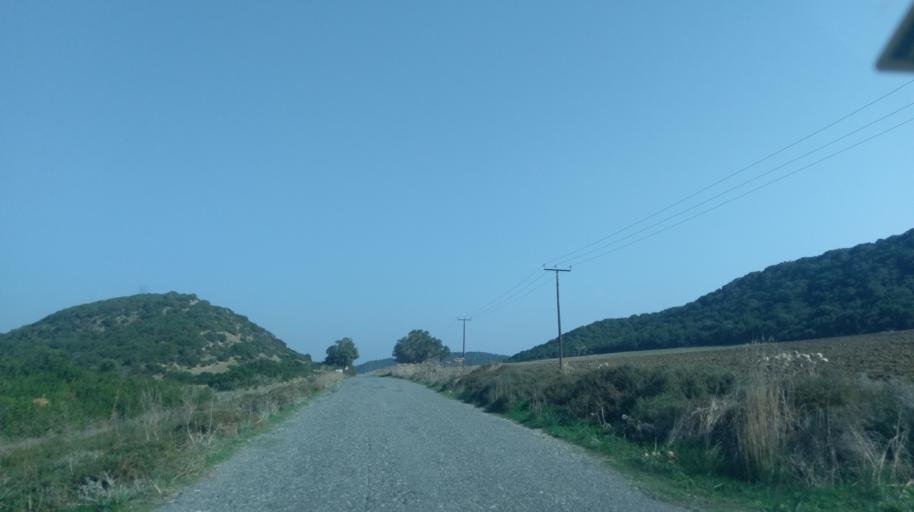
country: CY
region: Ammochostos
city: Rizokarpaso
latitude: 35.6327
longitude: 34.5002
